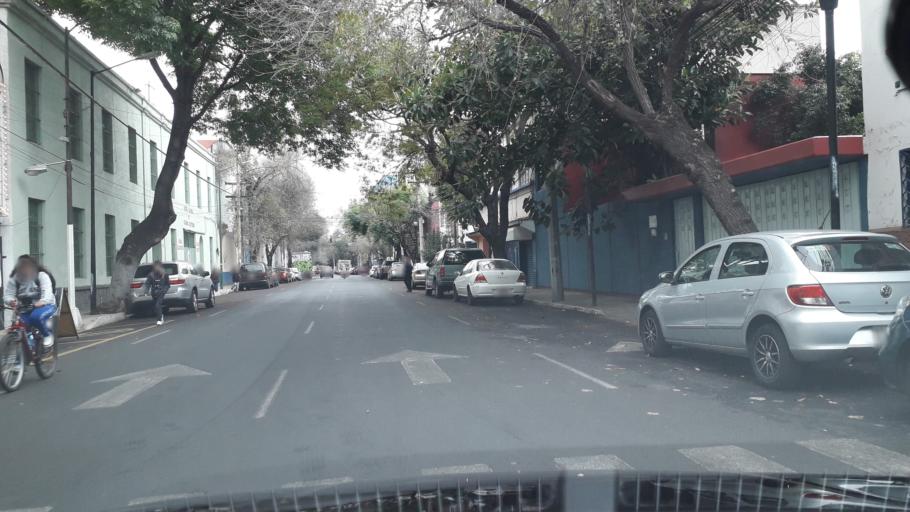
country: MX
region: Mexico City
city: Cuauhtemoc
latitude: 19.4457
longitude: -99.1606
